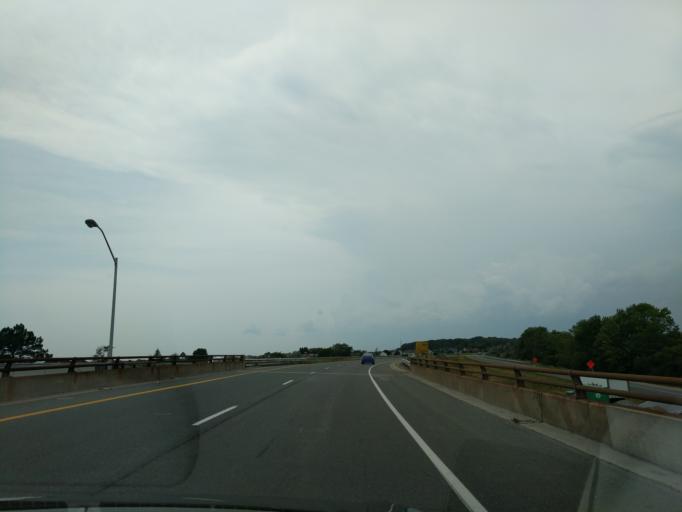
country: CA
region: Ontario
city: Thorold
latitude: 43.1148
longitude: -79.2153
